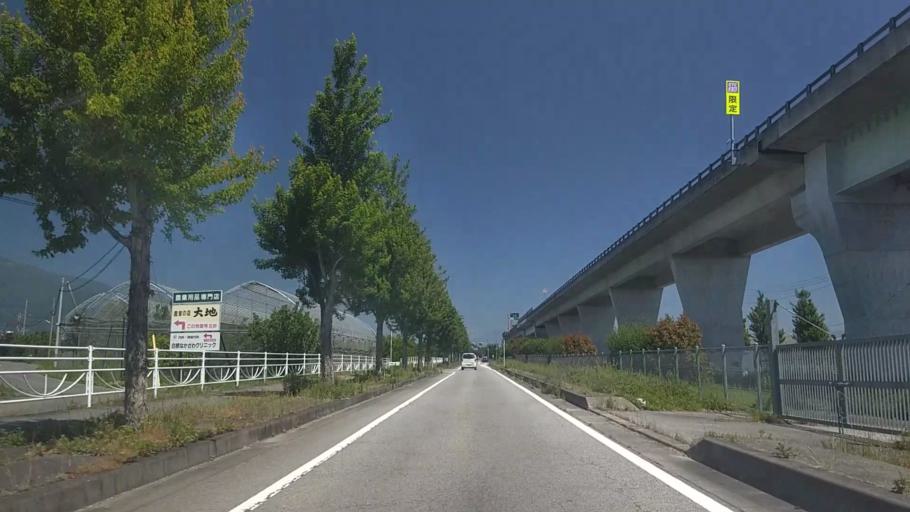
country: JP
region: Yamanashi
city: Ryuo
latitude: 35.6301
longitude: 138.4736
